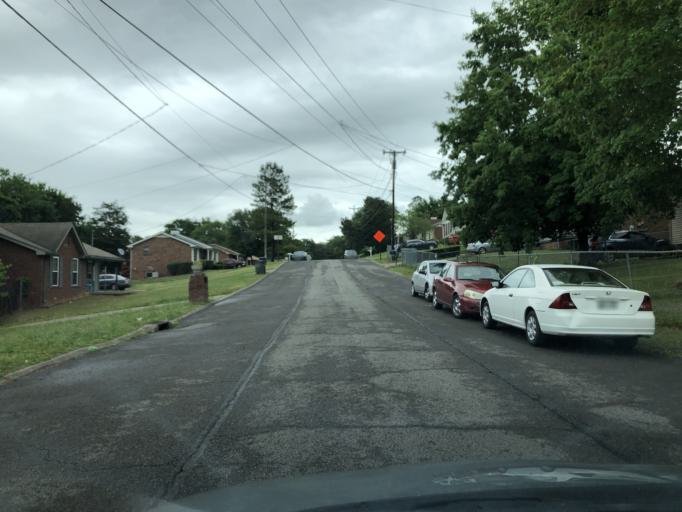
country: US
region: Tennessee
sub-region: Davidson County
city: Nashville
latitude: 36.2456
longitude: -86.7706
